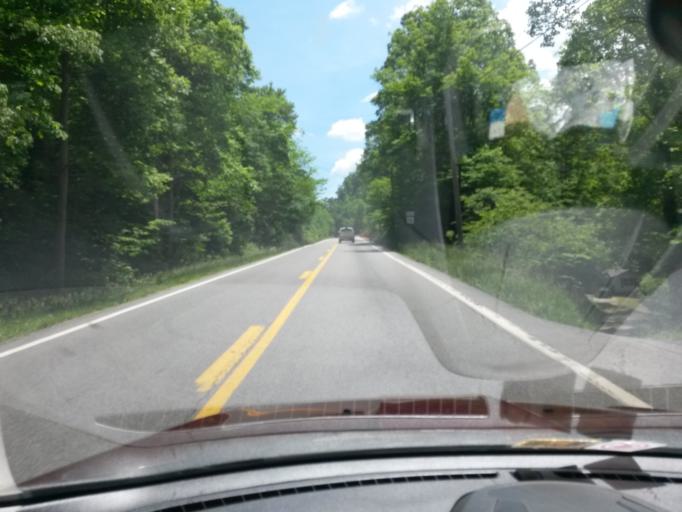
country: US
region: West Virginia
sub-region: Wyoming County
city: Pineville
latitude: 37.5523
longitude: -81.5563
